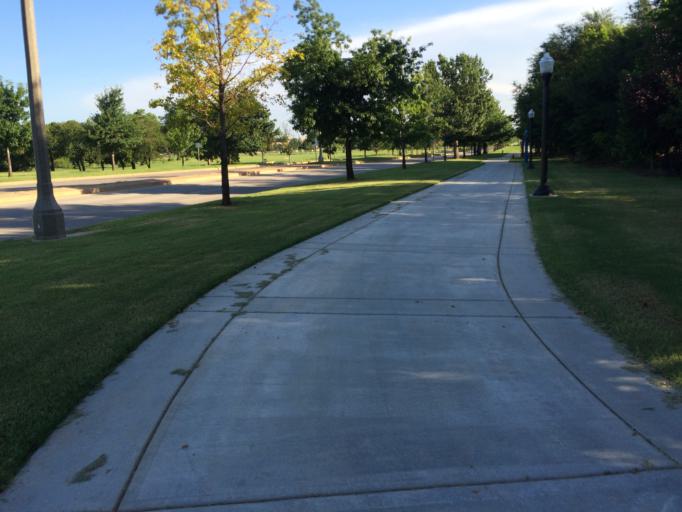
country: US
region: Oklahoma
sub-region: Cleveland County
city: Norman
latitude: 35.1813
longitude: -97.4412
